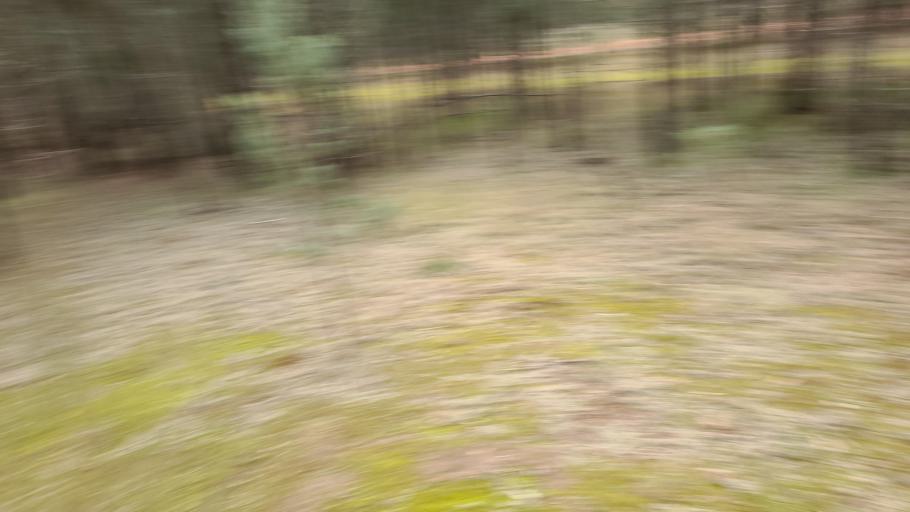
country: AU
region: New South Wales
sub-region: Coolamon
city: Coolamon
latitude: -34.8571
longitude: 146.9255
